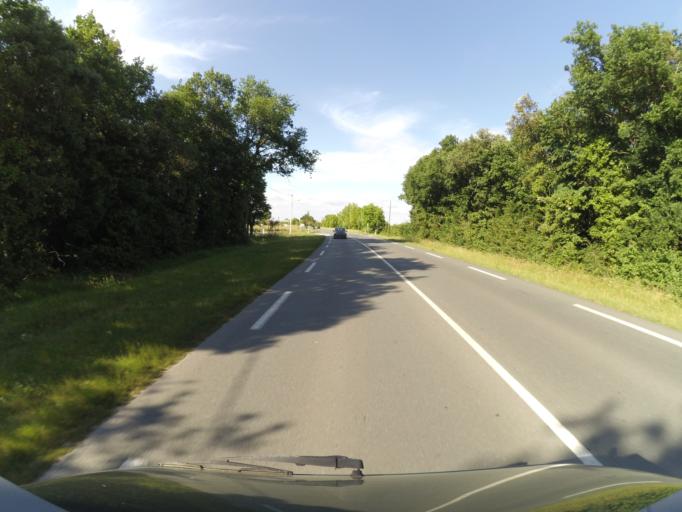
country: FR
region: Poitou-Charentes
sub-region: Departement de la Charente-Maritime
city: Le Gua
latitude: 45.7057
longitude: -0.9738
